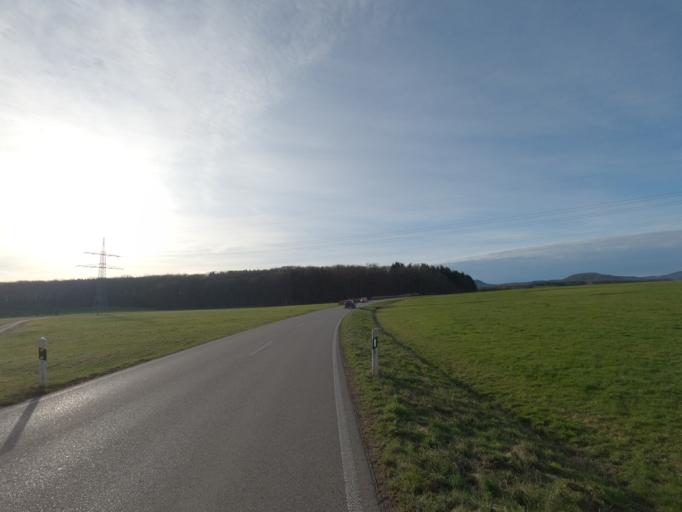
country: DE
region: Baden-Wuerttemberg
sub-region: Regierungsbezirk Stuttgart
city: Hattenhofen
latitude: 48.6766
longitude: 9.5924
